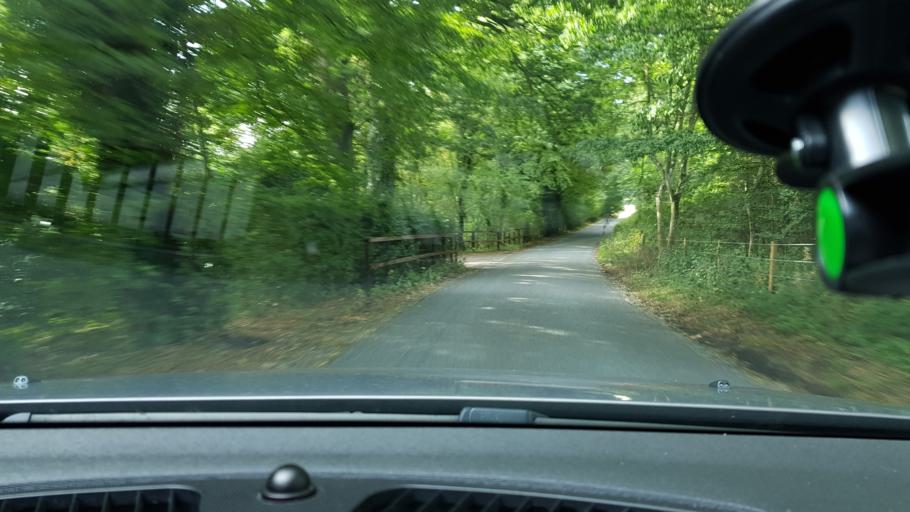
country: GB
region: England
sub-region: West Berkshire
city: Wickham
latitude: 51.4385
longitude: -1.4353
